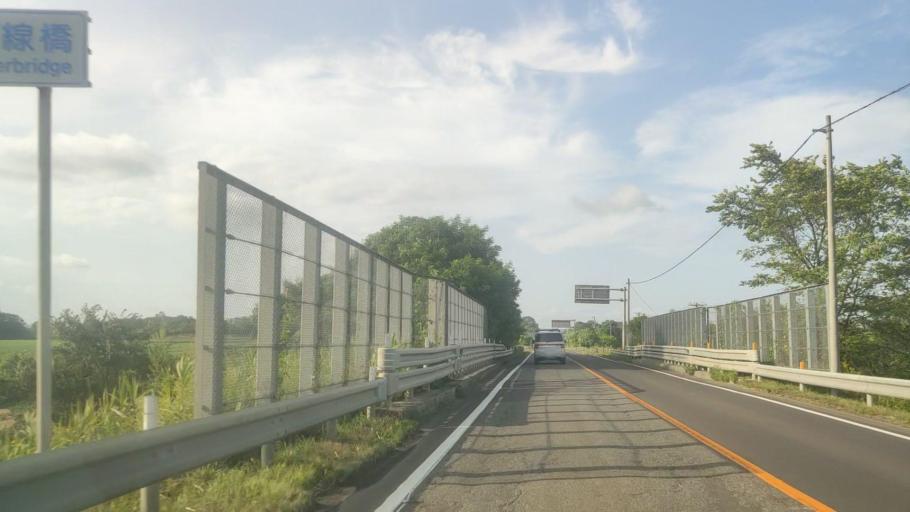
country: JP
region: Hokkaido
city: Chitose
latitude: 42.8883
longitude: 141.8124
